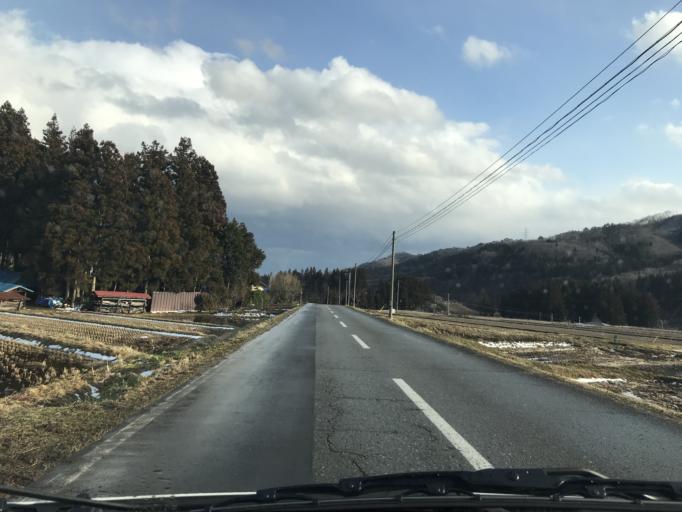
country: JP
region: Iwate
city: Mizusawa
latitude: 39.0808
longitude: 141.0025
